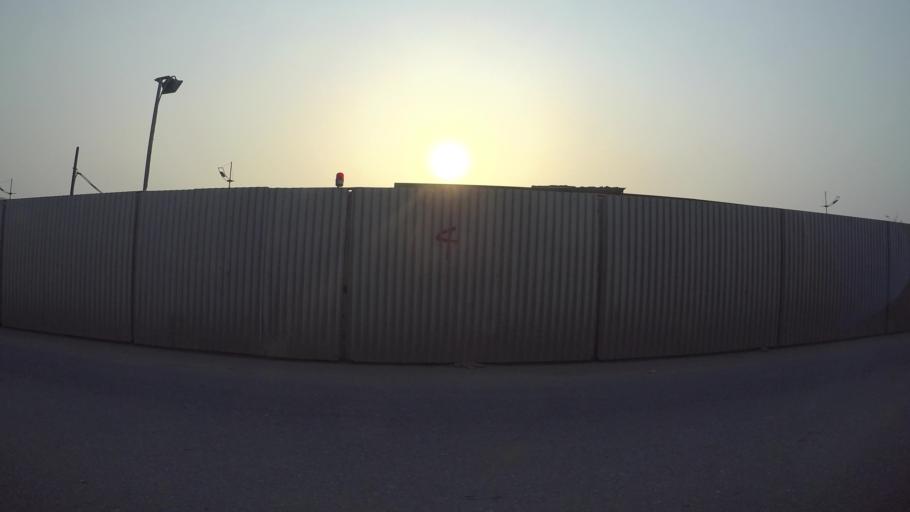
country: VN
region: Ha Noi
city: Tay Ho
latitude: 21.0744
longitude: 105.7859
